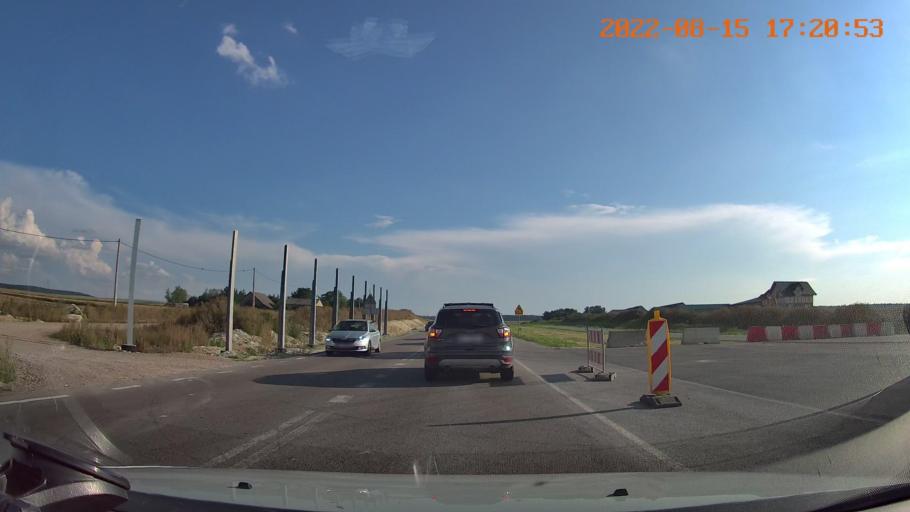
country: PL
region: Swietokrzyskie
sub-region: Powiat jedrzejowski
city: Wodzislaw
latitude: 50.4928
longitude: 20.1836
